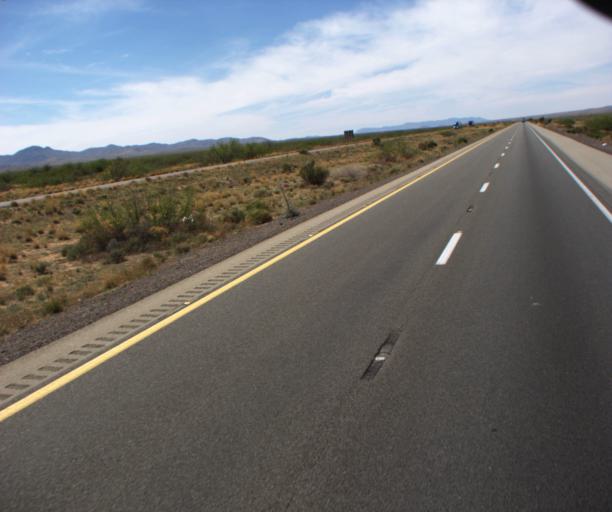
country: US
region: Arizona
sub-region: Cochise County
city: Willcox
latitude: 32.3408
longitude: -109.5634
